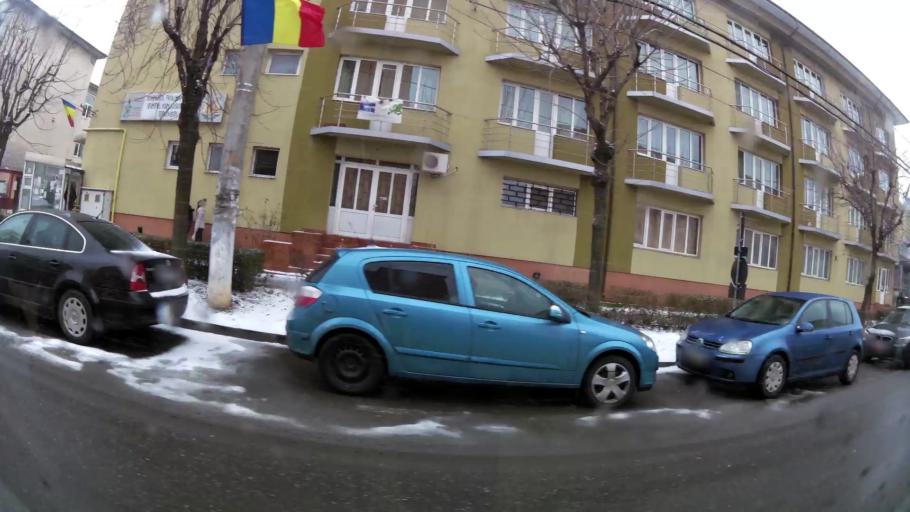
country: RO
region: Dambovita
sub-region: Municipiul Targoviste
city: Targoviste
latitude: 44.9214
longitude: 25.4479
